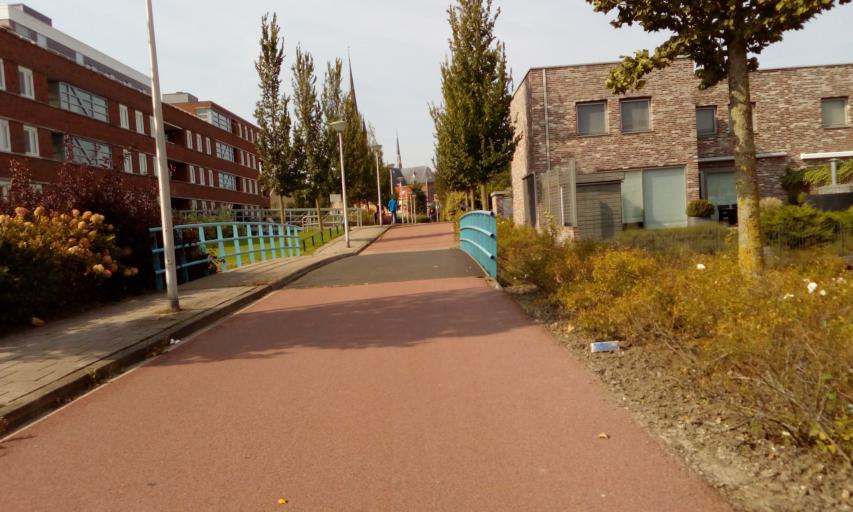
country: NL
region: South Holland
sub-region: Gemeente Westland
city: Kwintsheul
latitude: 52.0249
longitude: 4.2840
